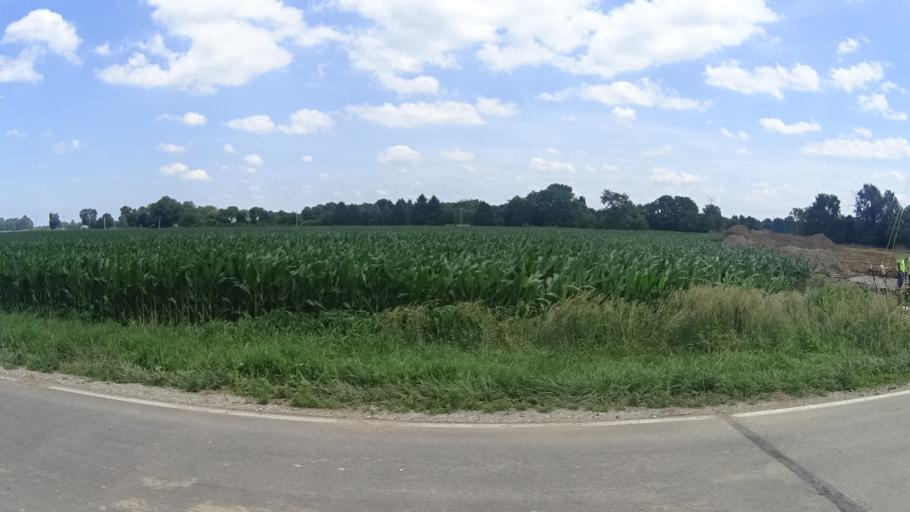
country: US
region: Ohio
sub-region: Erie County
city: Huron
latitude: 41.3382
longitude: -82.5362
